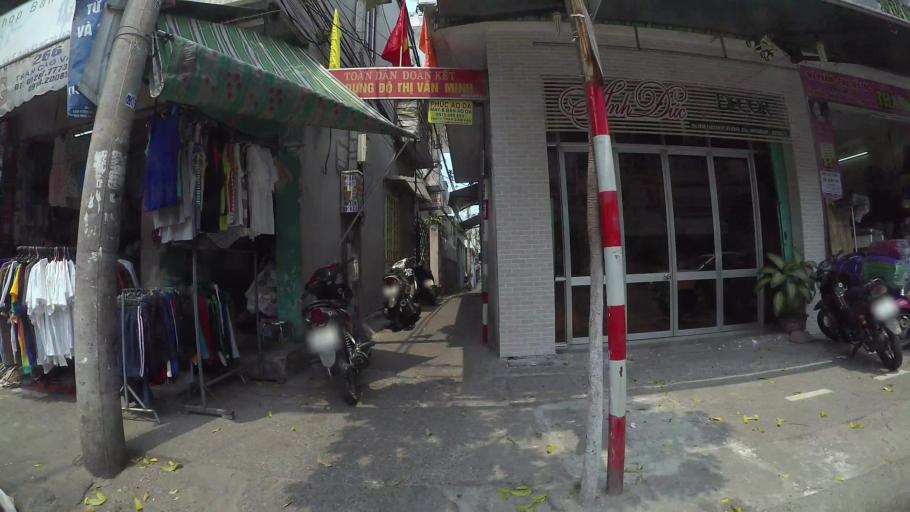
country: VN
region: Da Nang
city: Thanh Khe
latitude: 16.0717
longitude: 108.2048
